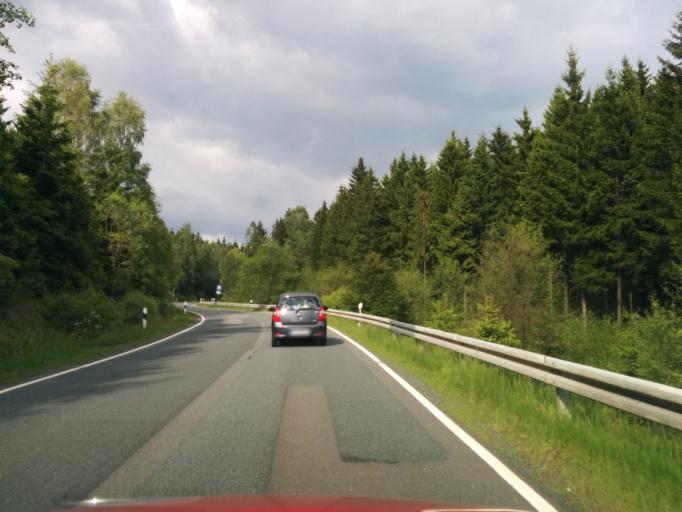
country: DE
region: Lower Saxony
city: Wieda
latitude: 51.6749
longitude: 10.5955
